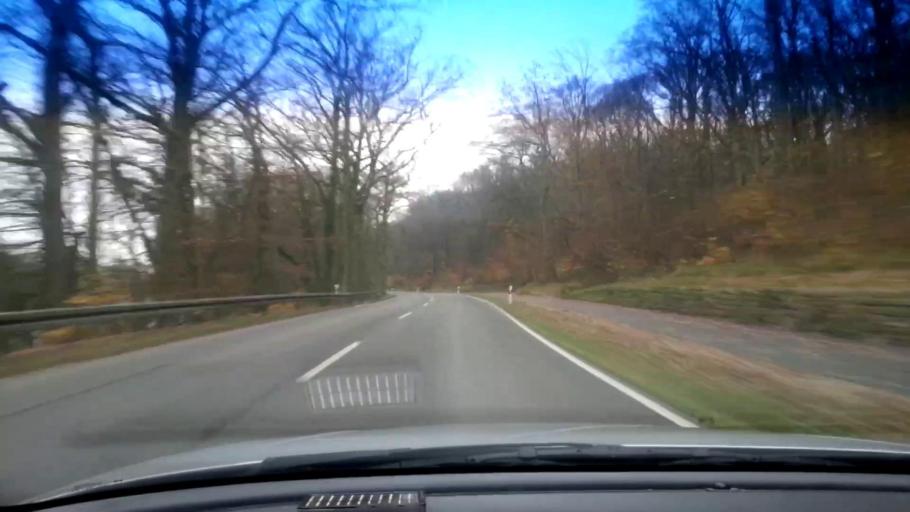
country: DE
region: Bavaria
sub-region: Upper Franconia
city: Pettstadt
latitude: 49.8528
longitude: 10.9253
